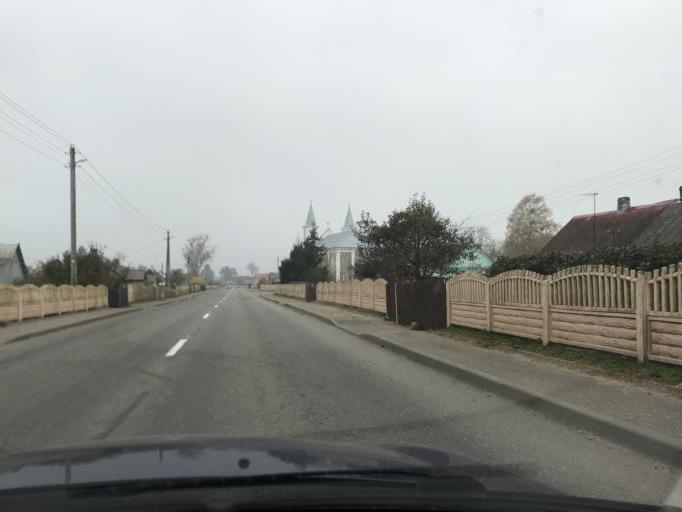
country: BY
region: Grodnenskaya
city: Hrodna
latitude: 53.8178
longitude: 23.8650
